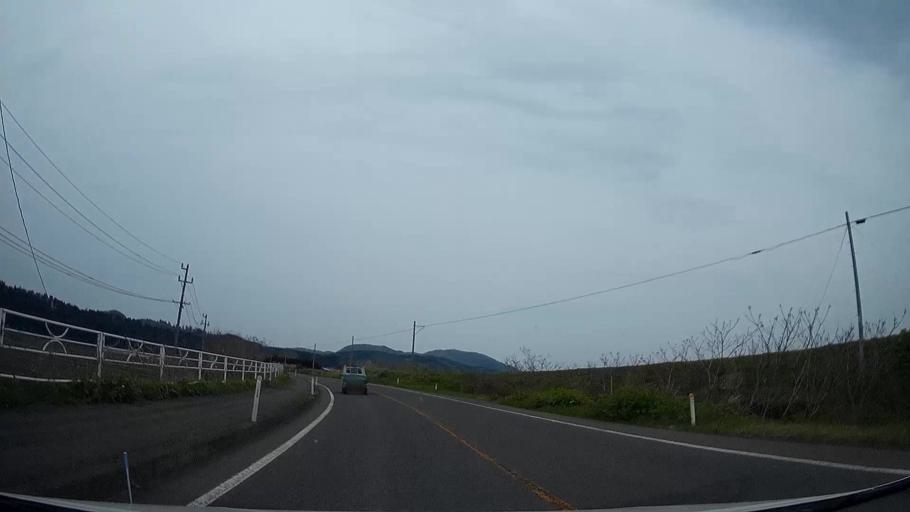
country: JP
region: Akita
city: Hanawa
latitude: 40.2772
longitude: 140.7998
